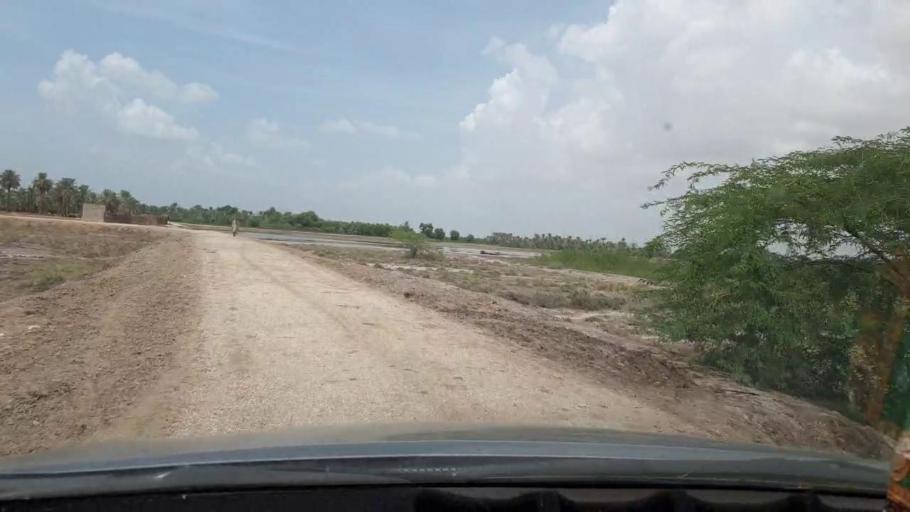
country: PK
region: Sindh
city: Khairpur
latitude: 27.4552
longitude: 68.8252
